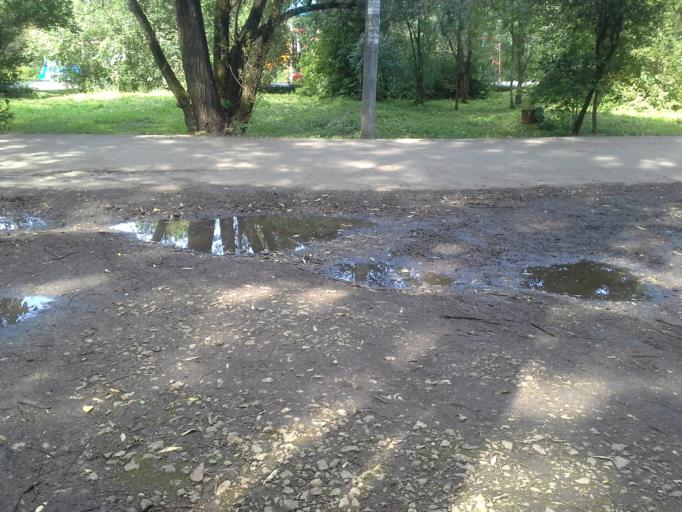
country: RU
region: Moskovskaya
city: Skolkovo
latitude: 55.6606
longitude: 37.3672
